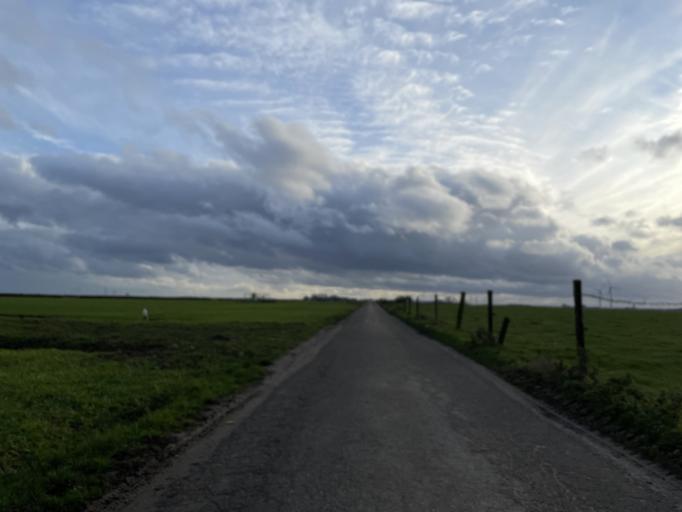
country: DE
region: North Rhine-Westphalia
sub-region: Regierungsbezirk Koln
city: Titz
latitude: 51.0810
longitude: 6.4169
